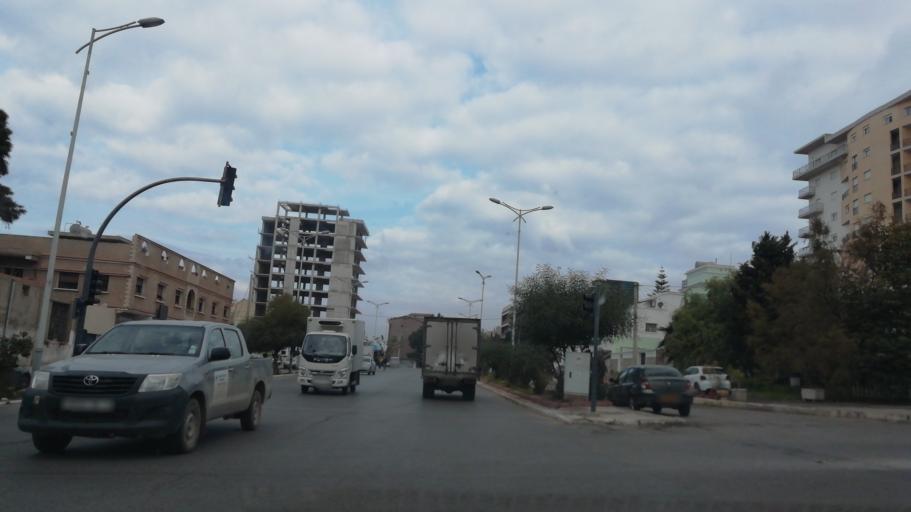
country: DZ
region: Oran
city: Oran
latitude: 35.7068
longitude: -0.6108
